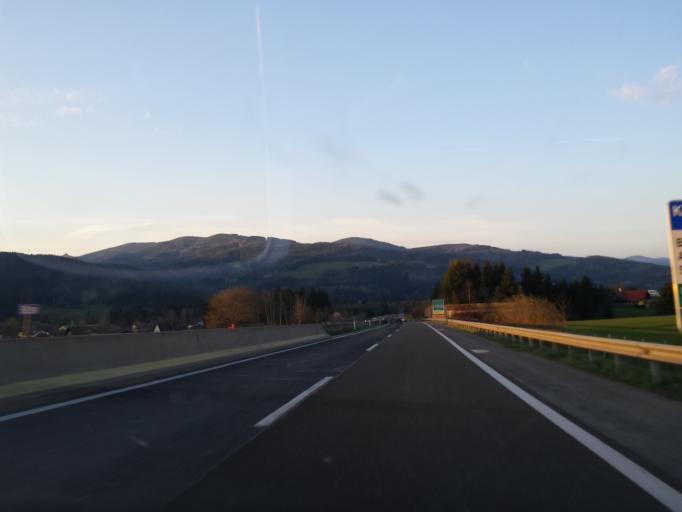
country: AT
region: Styria
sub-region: Politischer Bezirk Bruck-Muerzzuschlag
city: Krieglach
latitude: 47.5489
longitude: 15.5758
